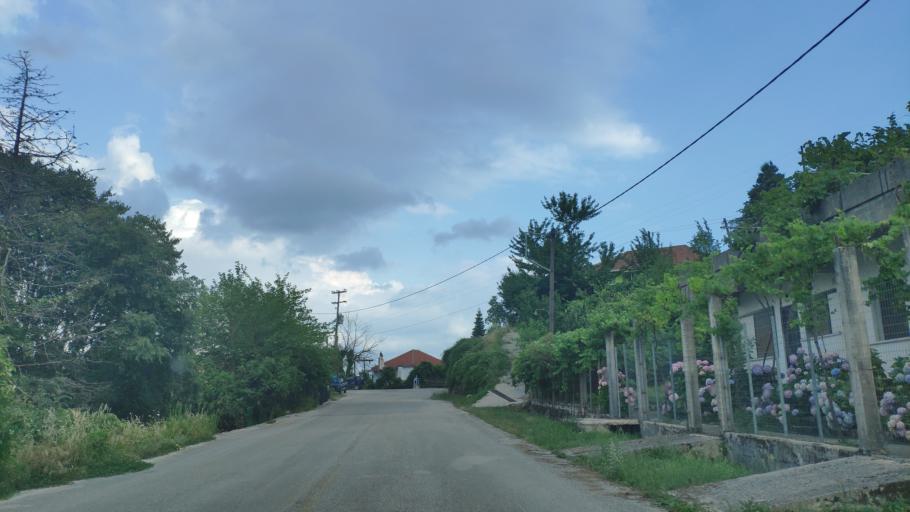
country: GR
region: Epirus
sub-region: Nomos Artas
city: Agios Dimitrios
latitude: 39.3936
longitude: 21.0202
